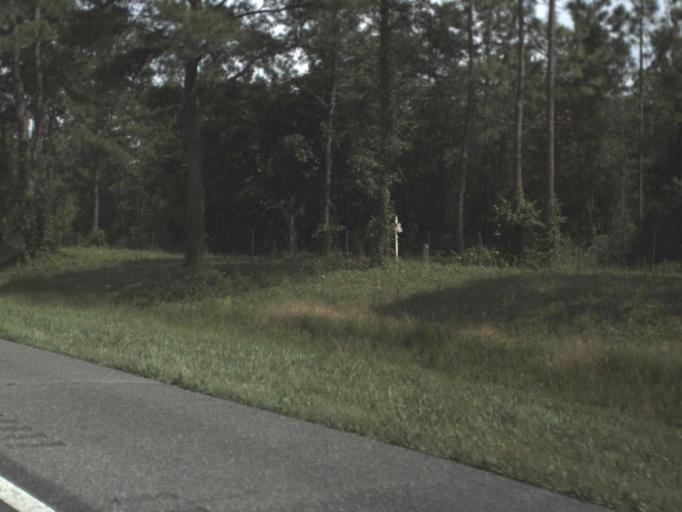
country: US
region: Florida
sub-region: Suwannee County
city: Wellborn
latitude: 30.2847
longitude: -82.8349
